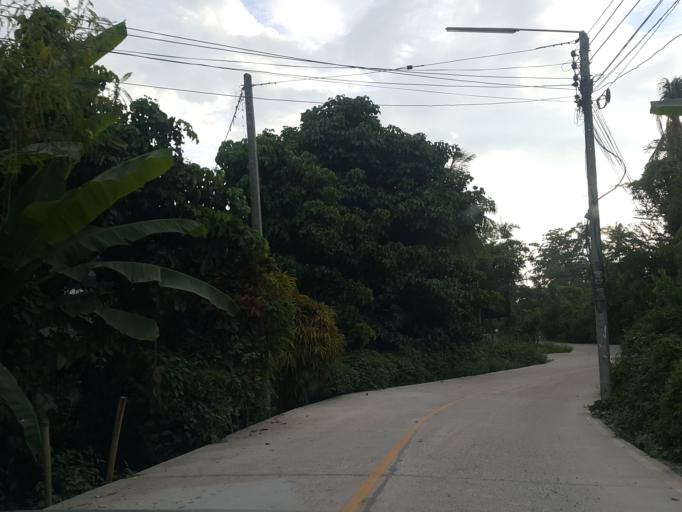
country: TH
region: Chiang Mai
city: San Sai
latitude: 18.8793
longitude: 99.0896
